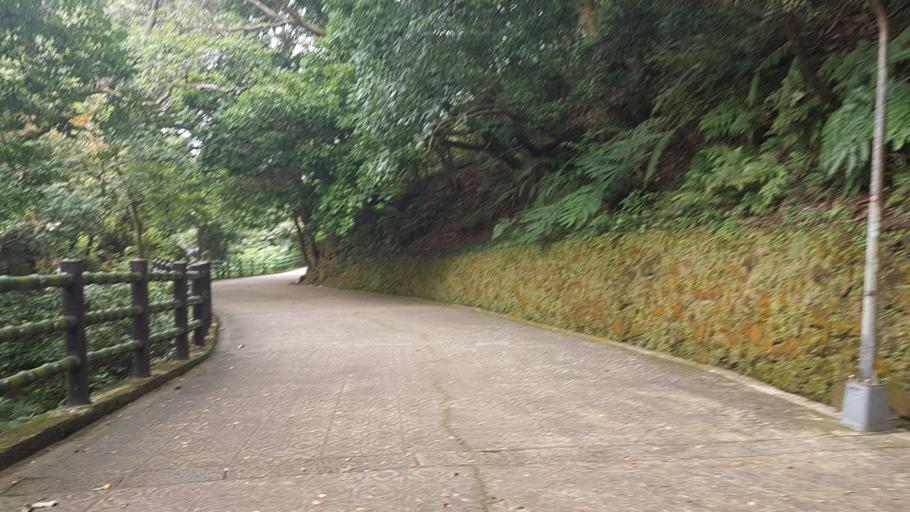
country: TW
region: Taipei
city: Taipei
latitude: 25.1523
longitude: 121.5404
